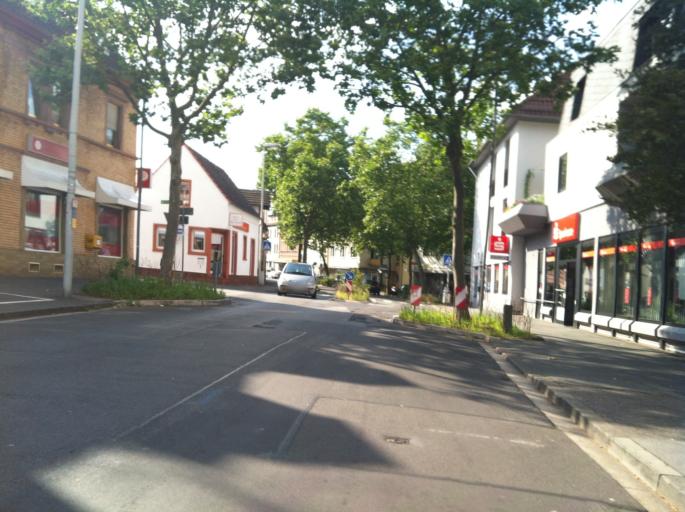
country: DE
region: Rheinland-Pfalz
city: Mainz
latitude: 50.0211
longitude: 8.2292
